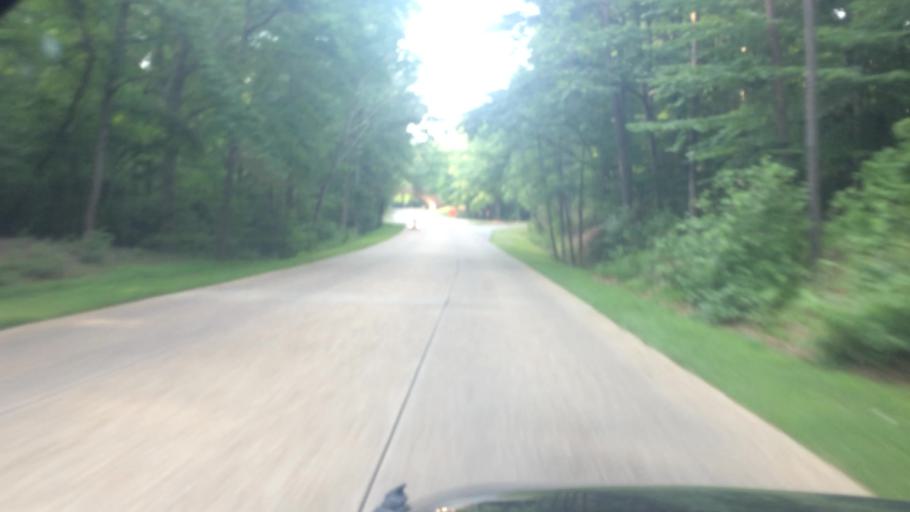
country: US
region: Virginia
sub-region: City of Williamsburg
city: Williamsburg
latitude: 37.2462
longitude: -76.6997
